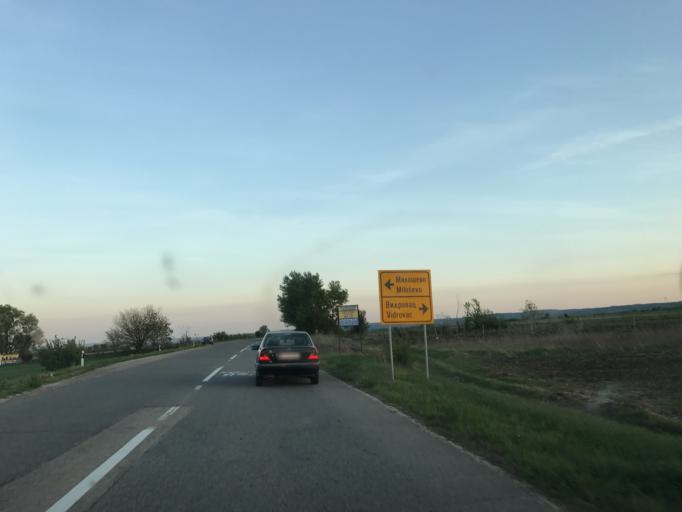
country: RS
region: Central Serbia
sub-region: Borski Okrug
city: Negotin
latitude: 44.2631
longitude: 22.5170
